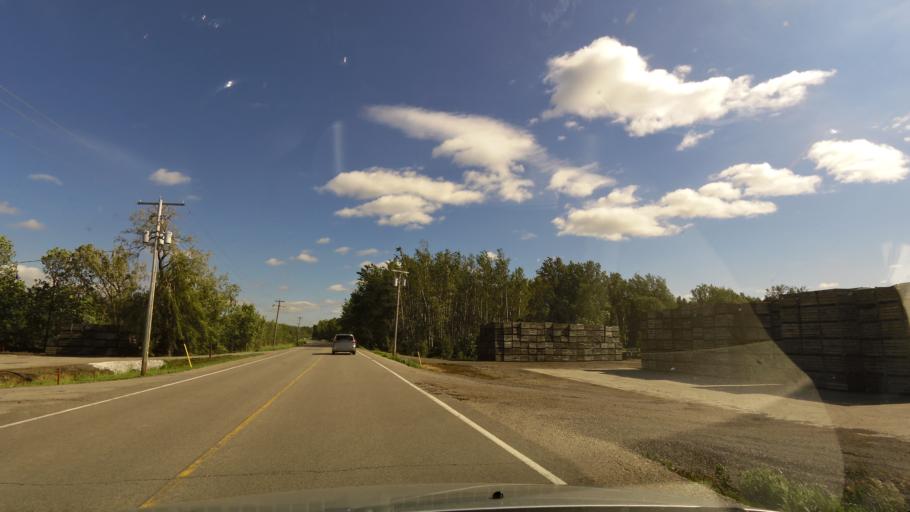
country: CA
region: Ontario
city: Innisfil
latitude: 44.2133
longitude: -79.6299
